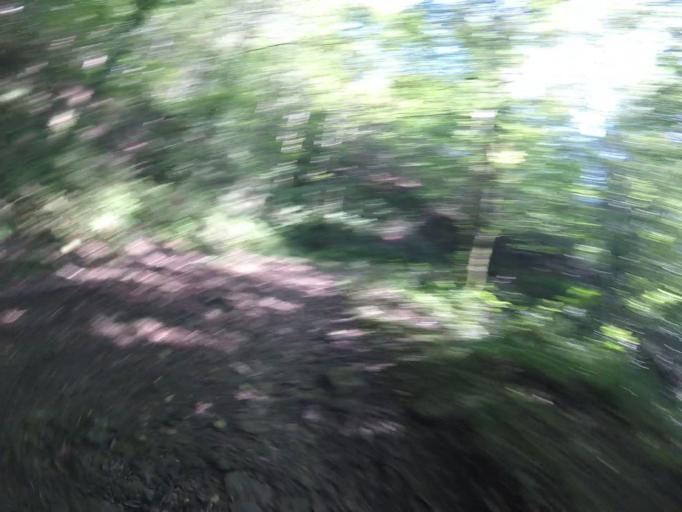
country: ES
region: Navarre
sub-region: Provincia de Navarra
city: Arano
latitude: 43.2444
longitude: -1.9011
